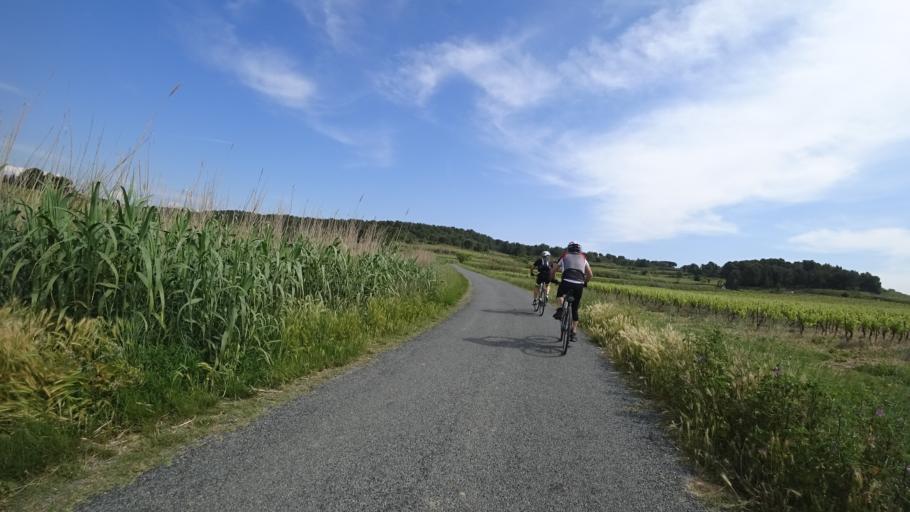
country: FR
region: Languedoc-Roussillon
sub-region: Departement de l'Aude
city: Canet
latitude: 43.2525
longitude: 2.8025
